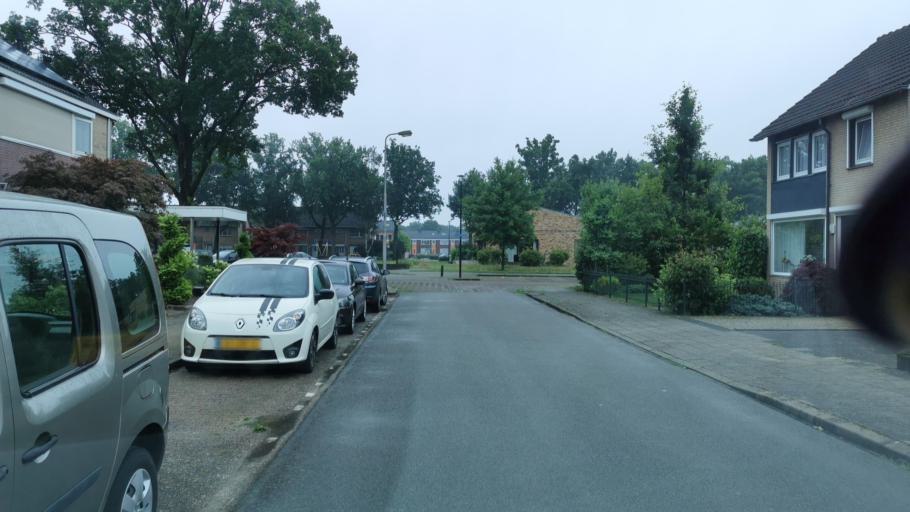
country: DE
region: North Rhine-Westphalia
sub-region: Regierungsbezirk Munster
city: Gronau
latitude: 52.2356
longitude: 7.0326
